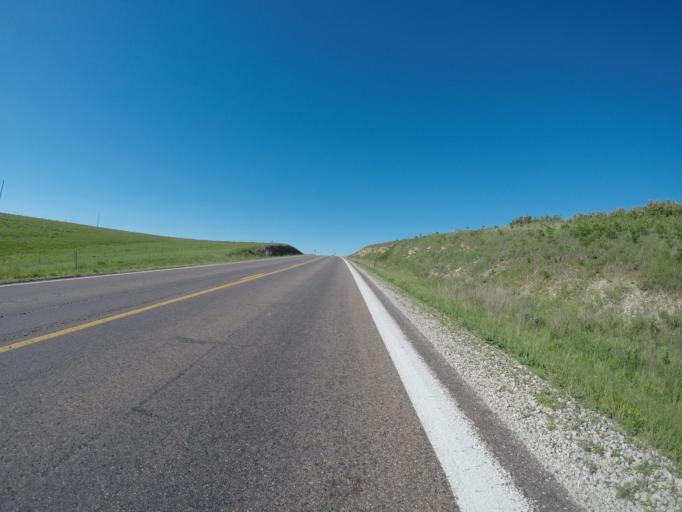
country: US
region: Kansas
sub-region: Morris County
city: Council Grove
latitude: 38.5677
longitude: -96.5213
